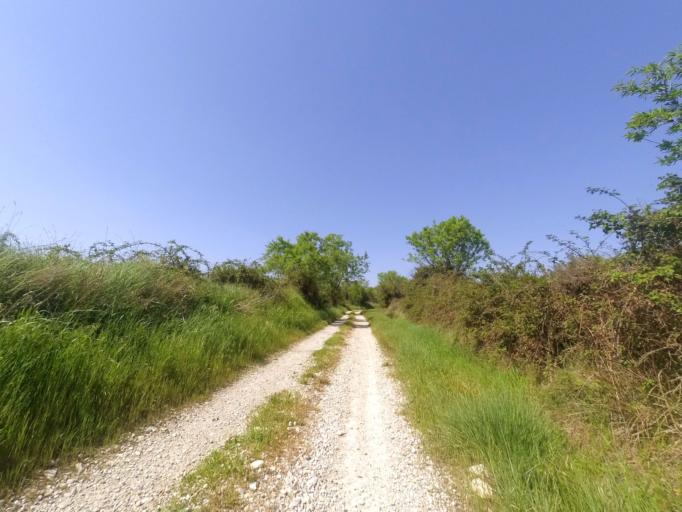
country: FR
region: Languedoc-Roussillon
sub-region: Departement du Gard
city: Congenies
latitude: 43.7761
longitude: 4.1677
